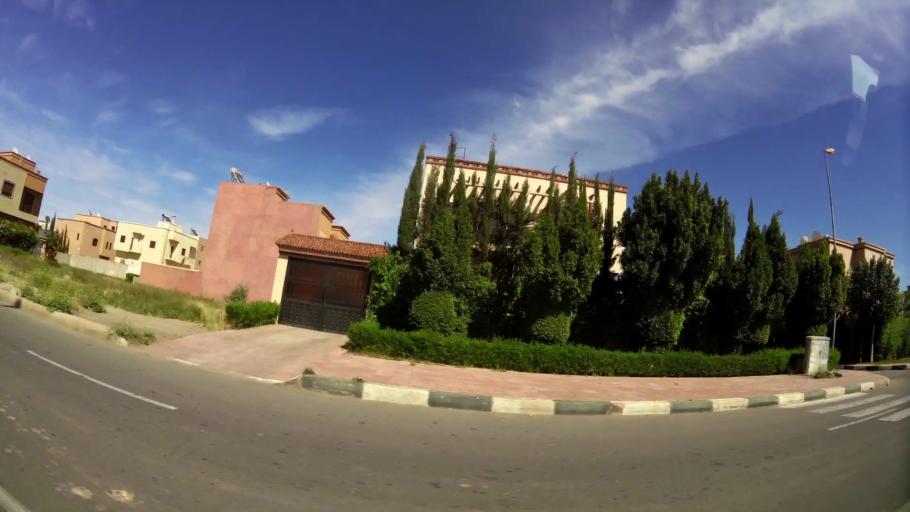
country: MA
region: Marrakech-Tensift-Al Haouz
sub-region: Marrakech
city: Marrakesh
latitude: 31.6563
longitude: -8.0597
